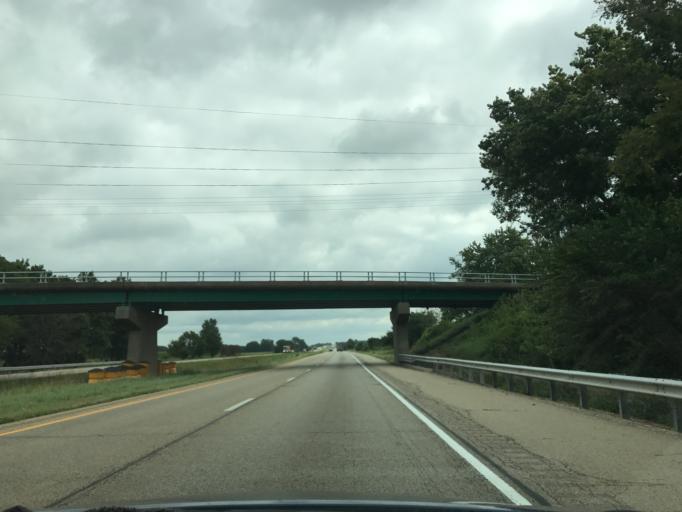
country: US
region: Illinois
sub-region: Henry County
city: Kewanee
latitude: 41.3863
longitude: -89.7670
